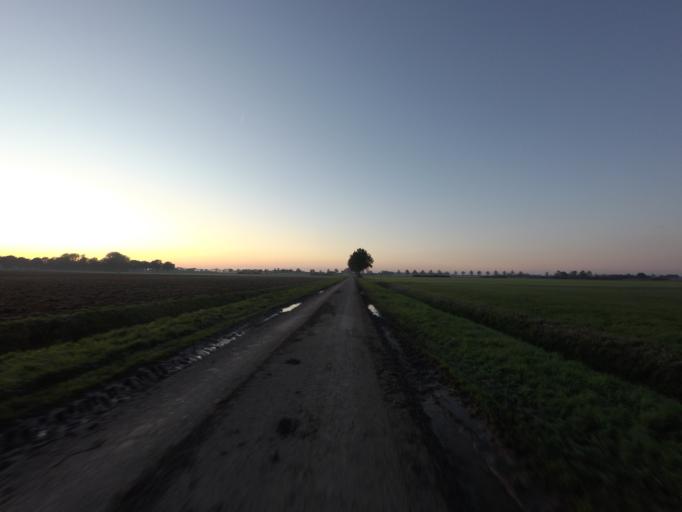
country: NL
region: North Brabant
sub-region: Gemeente Woudrichem
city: Almkerk
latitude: 51.7850
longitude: 4.9714
